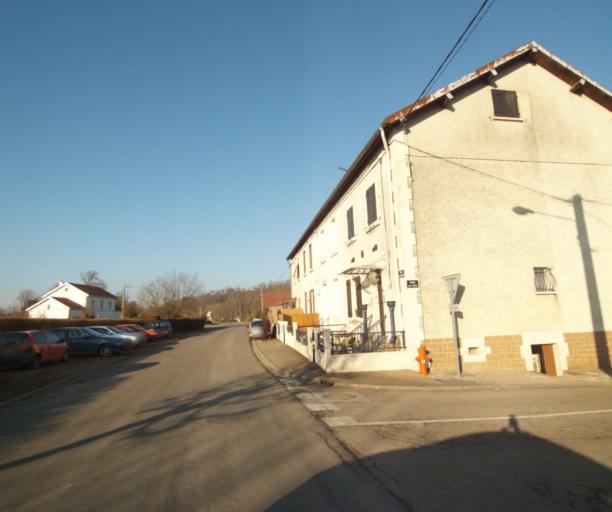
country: FR
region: Champagne-Ardenne
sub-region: Departement de la Haute-Marne
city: Bienville
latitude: 48.5821
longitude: 5.0454
